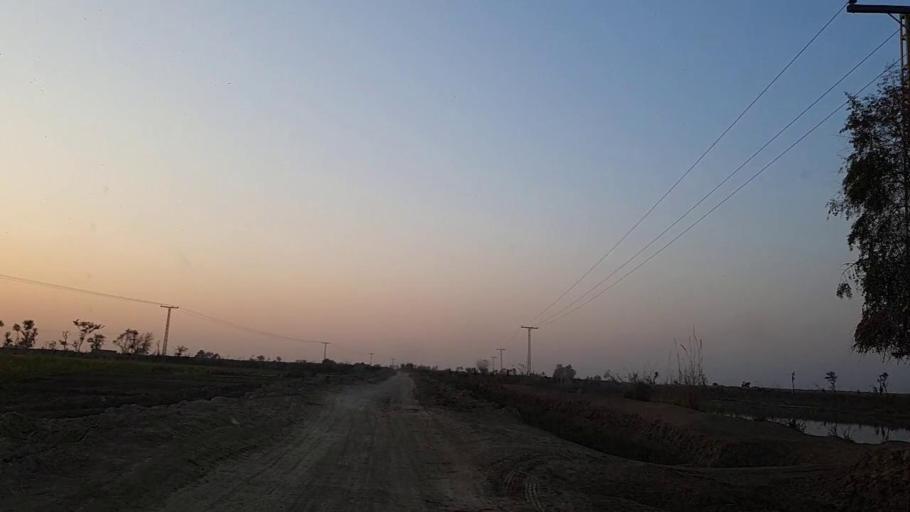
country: PK
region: Sindh
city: Bhit Shah
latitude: 25.9290
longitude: 68.4786
